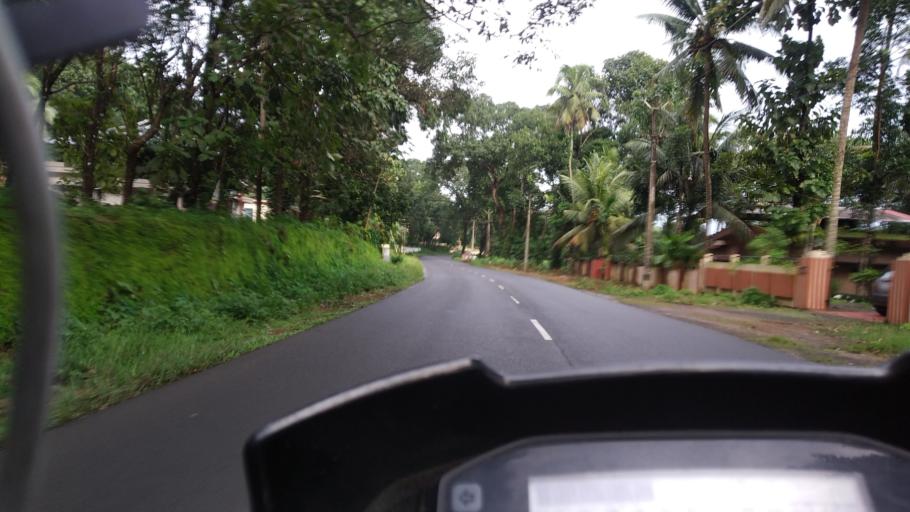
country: IN
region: Kerala
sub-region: Ernakulam
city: Kotamangalam
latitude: 10.0575
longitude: 76.6939
